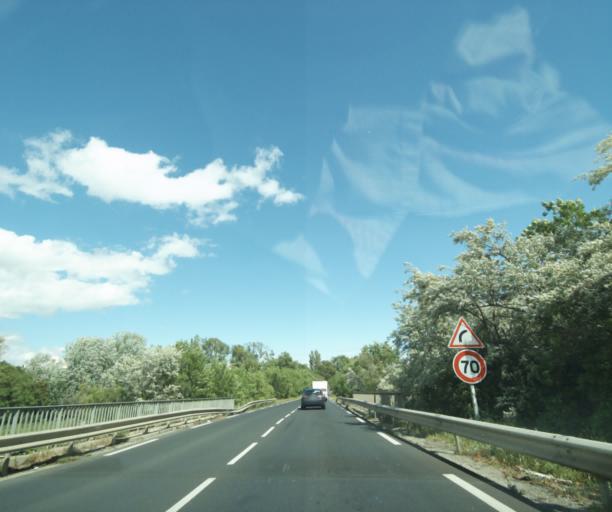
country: FR
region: Languedoc-Roussillon
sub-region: Departement de l'Herault
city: Saint-Jean-de-Vedas
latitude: 43.5855
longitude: 3.8428
